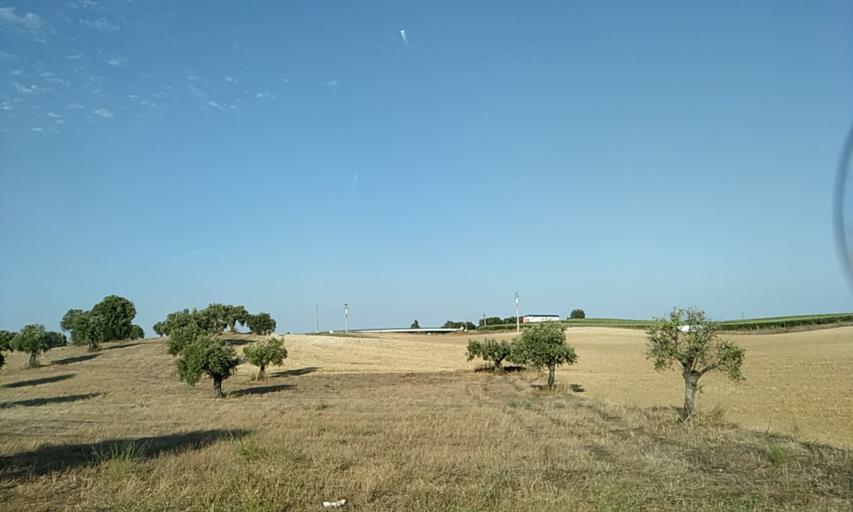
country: PT
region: Santarem
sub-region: Santarem
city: Santarem
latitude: 39.3274
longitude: -8.6625
